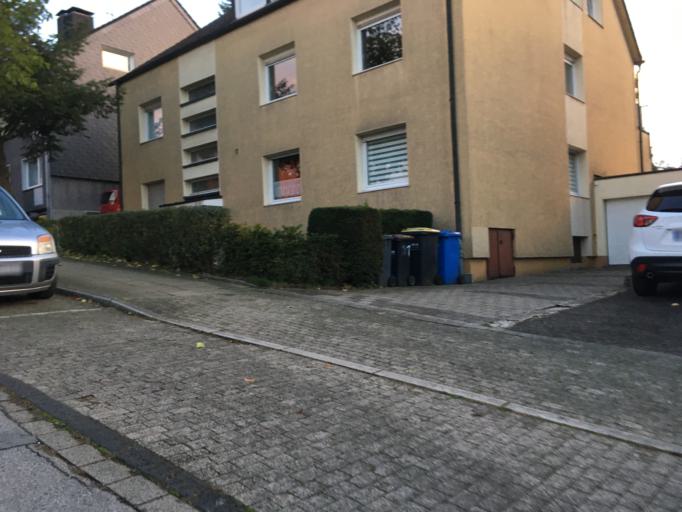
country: DE
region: North Rhine-Westphalia
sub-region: Regierungsbezirk Munster
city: Bottrop
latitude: 51.4824
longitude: 6.9288
